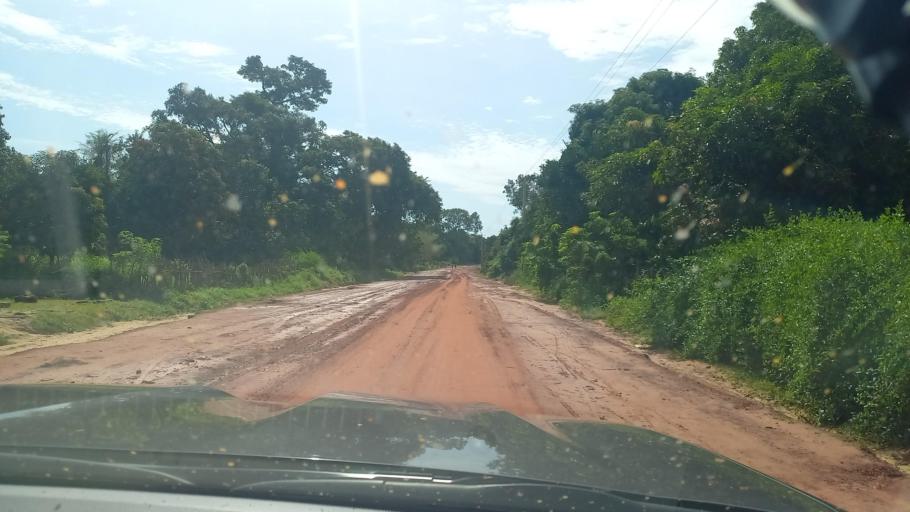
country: SN
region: Ziguinchor
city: Ziguinchor
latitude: 12.6739
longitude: -16.1928
